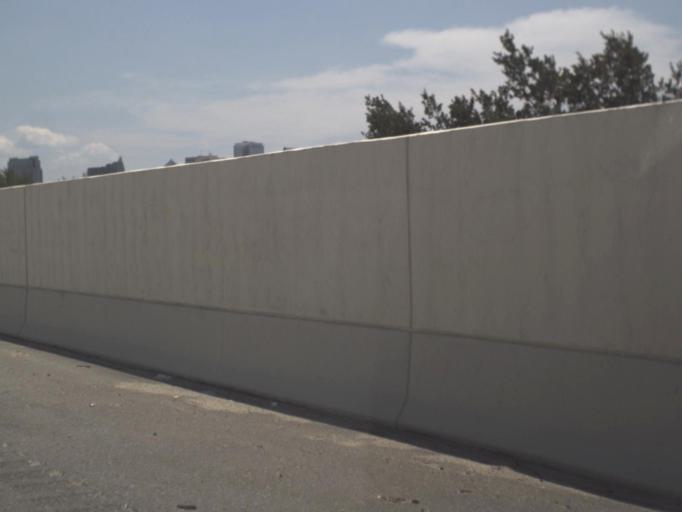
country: US
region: Florida
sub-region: Hillsborough County
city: Tampa
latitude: 27.9554
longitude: -82.4750
